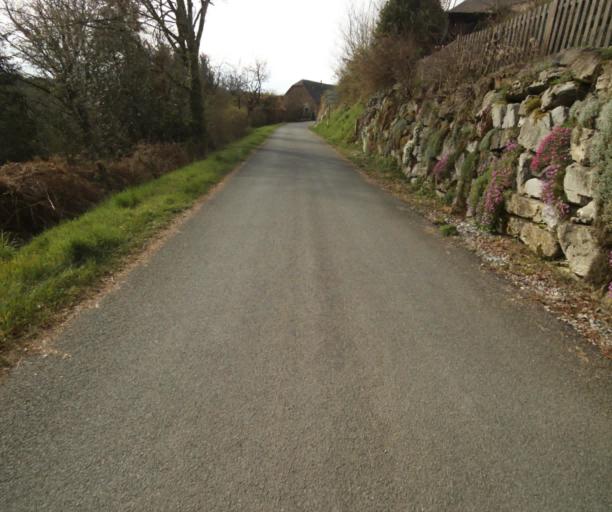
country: FR
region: Limousin
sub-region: Departement de la Correze
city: Correze
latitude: 45.4228
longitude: 1.8030
